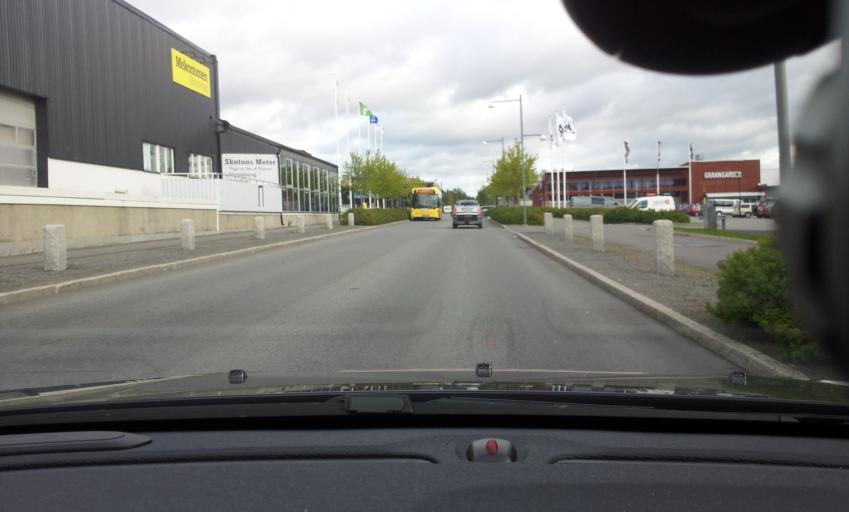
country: SE
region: Jaemtland
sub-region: OEstersunds Kommun
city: Ostersund
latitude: 63.1631
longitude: 14.6517
